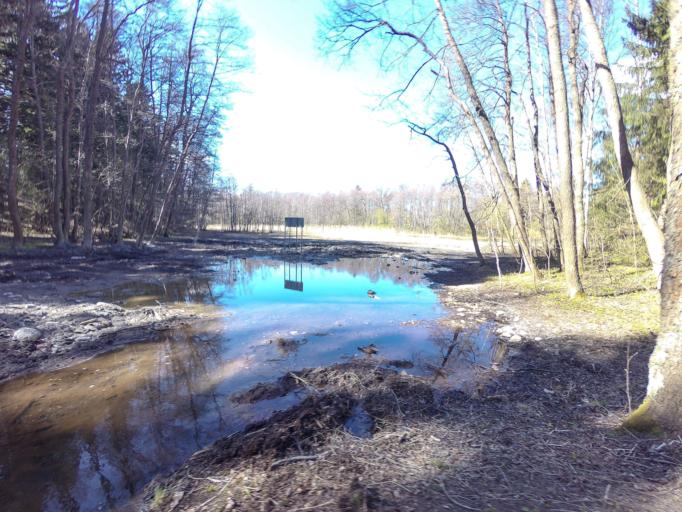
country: FI
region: Uusimaa
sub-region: Helsinki
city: Vantaa
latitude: 60.1718
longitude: 25.0620
